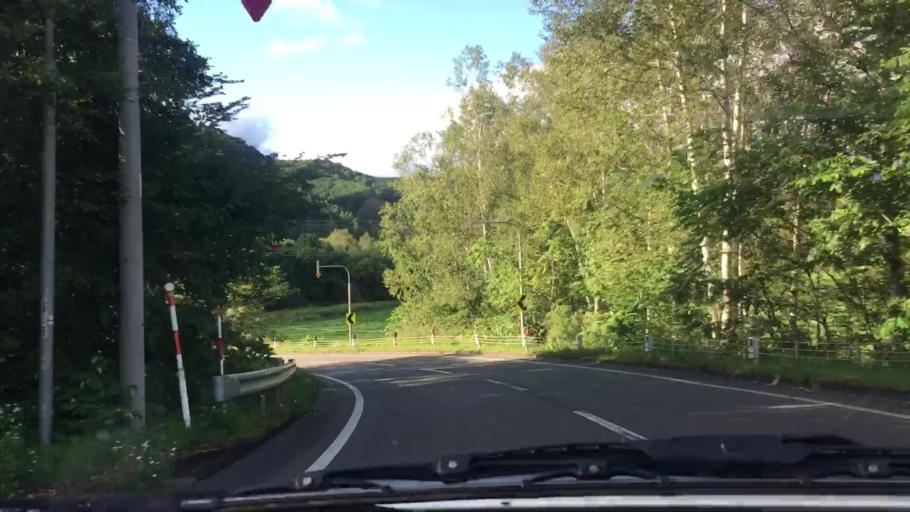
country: JP
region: Hokkaido
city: Otofuke
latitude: 43.1819
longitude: 142.9293
